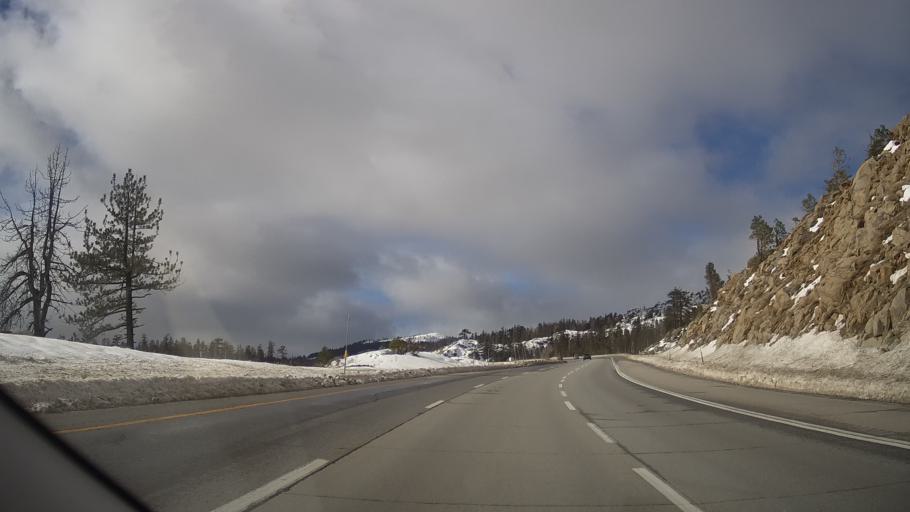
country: US
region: California
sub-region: Nevada County
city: Truckee
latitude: 39.3418
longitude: -120.3216
